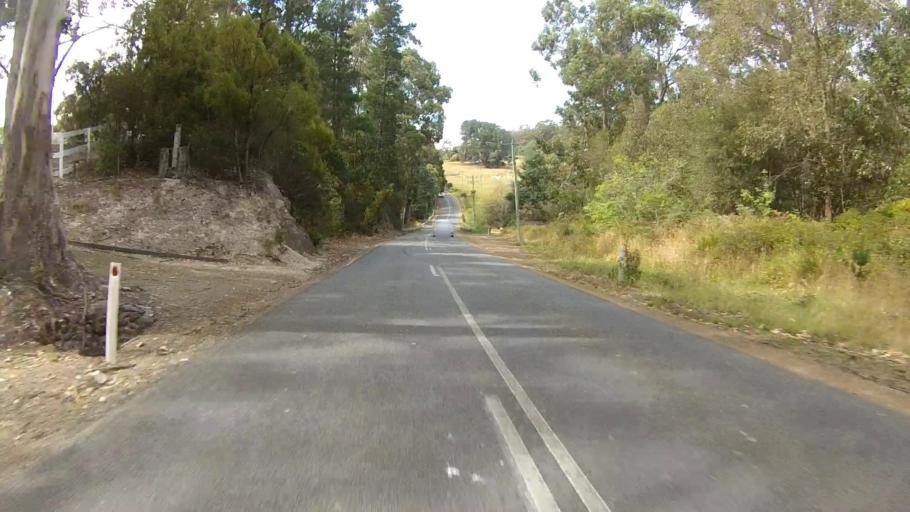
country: AU
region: Tasmania
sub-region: Kingborough
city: Kettering
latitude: -43.1808
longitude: 147.2387
